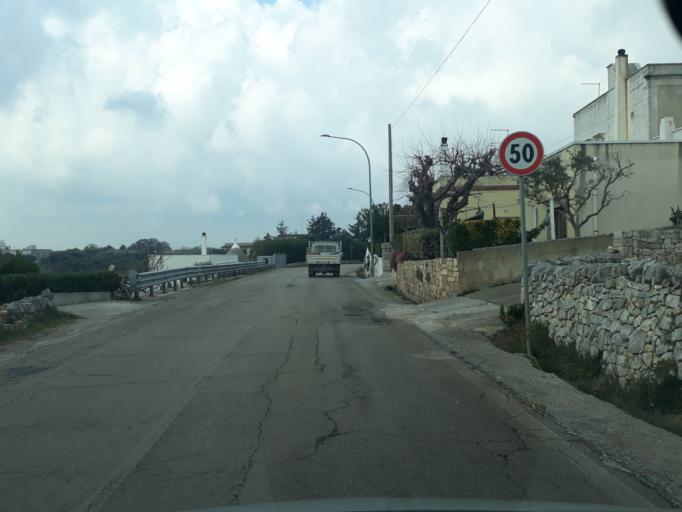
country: IT
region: Apulia
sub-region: Provincia di Brindisi
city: Cisternino
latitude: 40.7451
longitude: 17.3986
